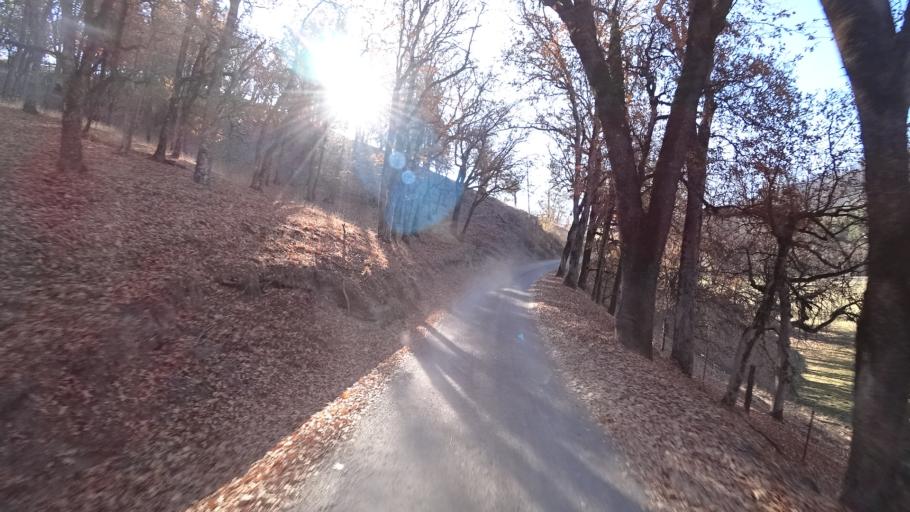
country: US
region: California
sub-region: Siskiyou County
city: Happy Camp
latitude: 41.8344
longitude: -123.0058
